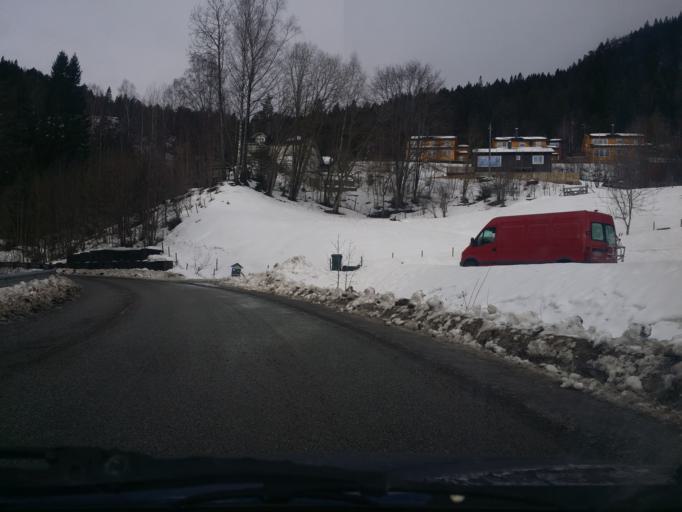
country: NO
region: Buskerud
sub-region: Lier
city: Lierbyen
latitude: 59.8215
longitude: 10.2003
